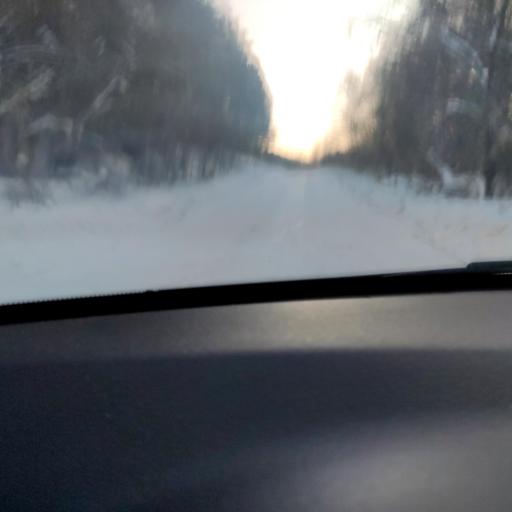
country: RU
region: Perm
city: Perm
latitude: 57.9961
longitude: 56.3462
